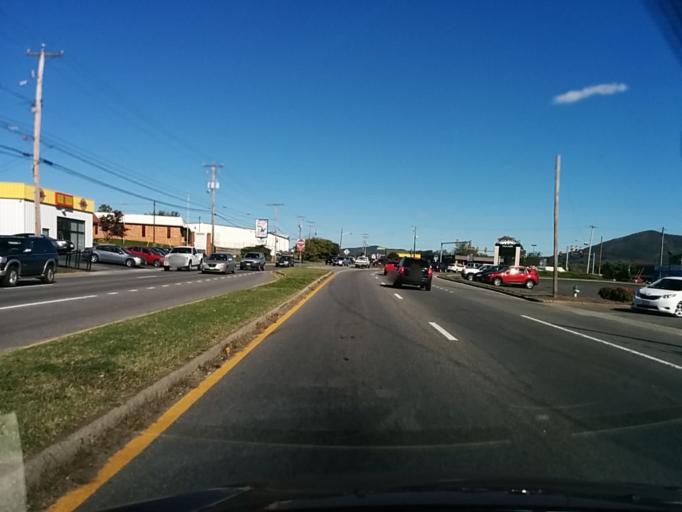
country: US
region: Virginia
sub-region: Roanoke County
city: Hollins
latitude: 37.3460
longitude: -79.9572
